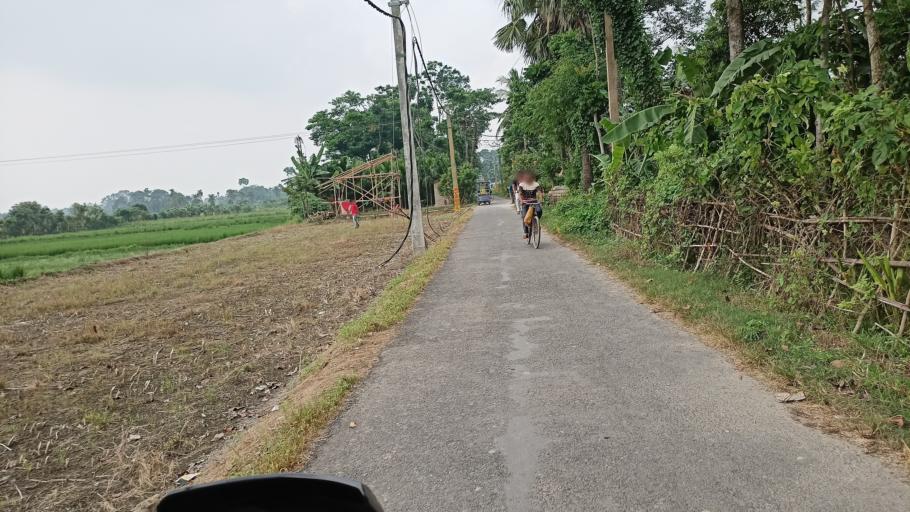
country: IN
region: West Bengal
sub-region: North 24 Parganas
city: Bangaon
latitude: 23.0628
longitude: 88.8207
